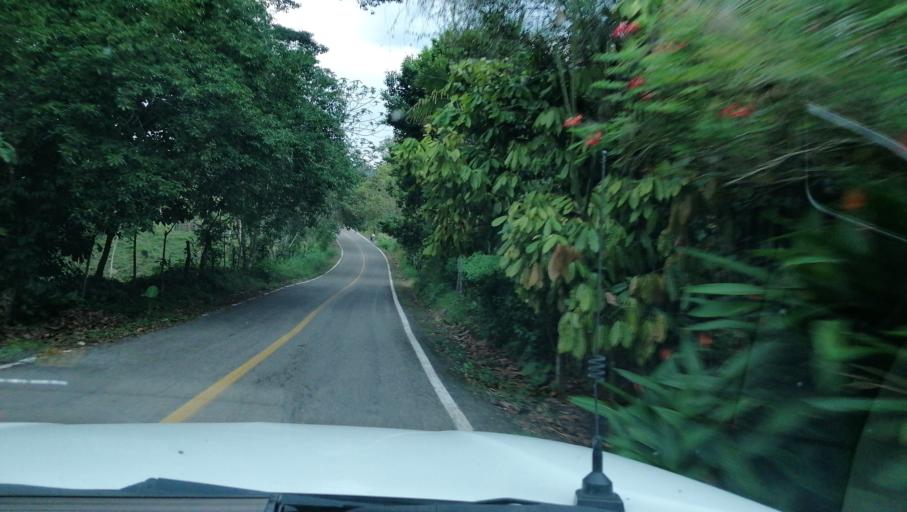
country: MX
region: Chiapas
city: Pichucalco
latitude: 17.5225
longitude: -93.1532
